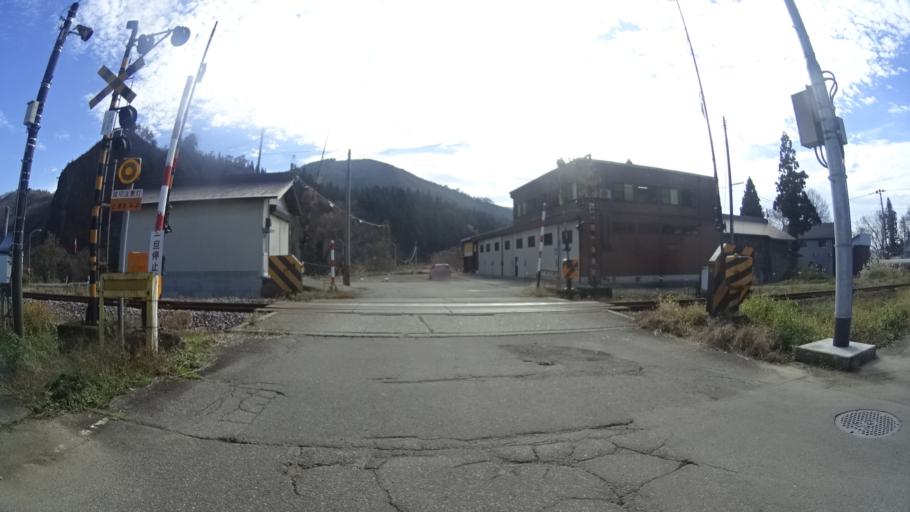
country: JP
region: Niigata
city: Tochio-honcho
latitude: 37.3033
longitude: 139.0011
